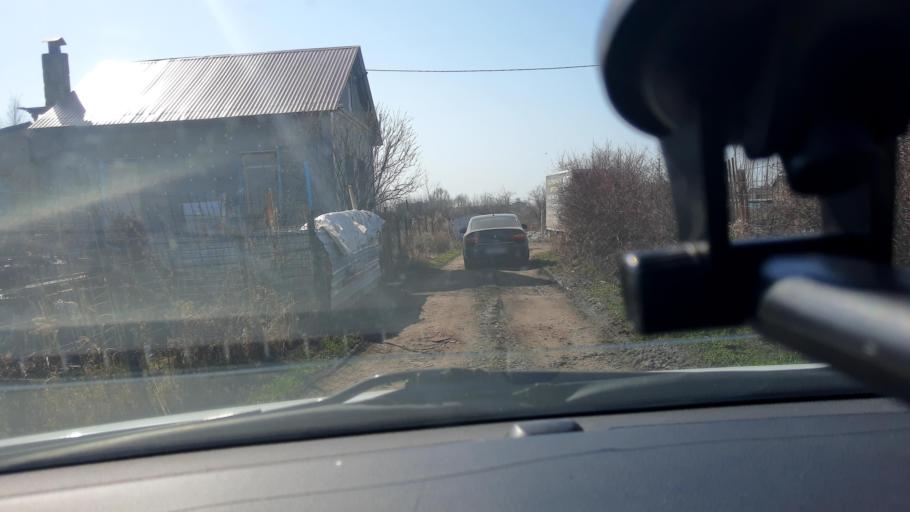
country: RU
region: Bashkortostan
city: Mikhaylovka
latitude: 54.7222
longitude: 55.8274
